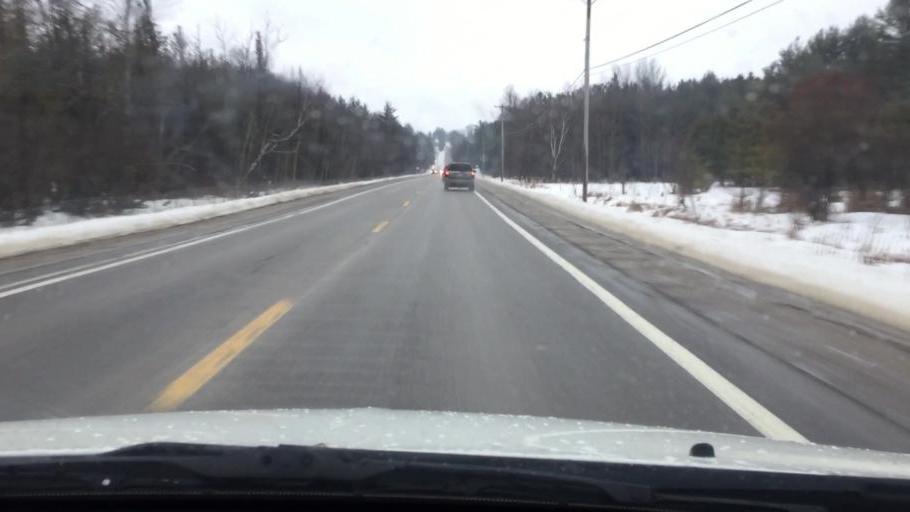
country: US
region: Michigan
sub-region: Charlevoix County
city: East Jordan
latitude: 45.2333
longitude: -85.1817
